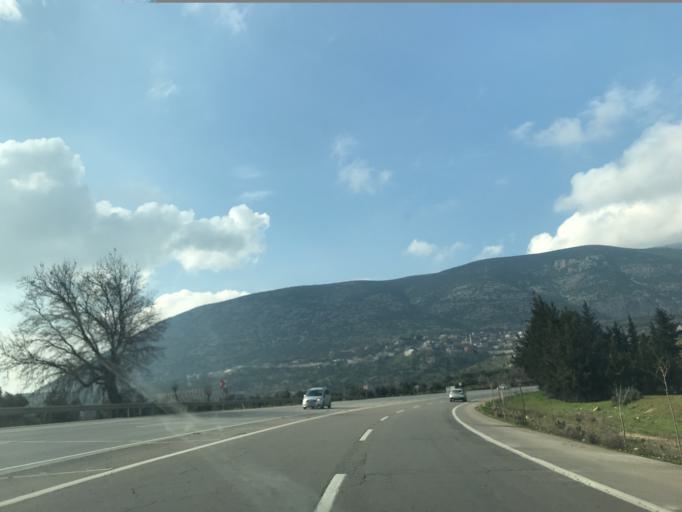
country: TR
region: Hatay
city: Kirikhan
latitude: 36.4754
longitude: 36.2783
